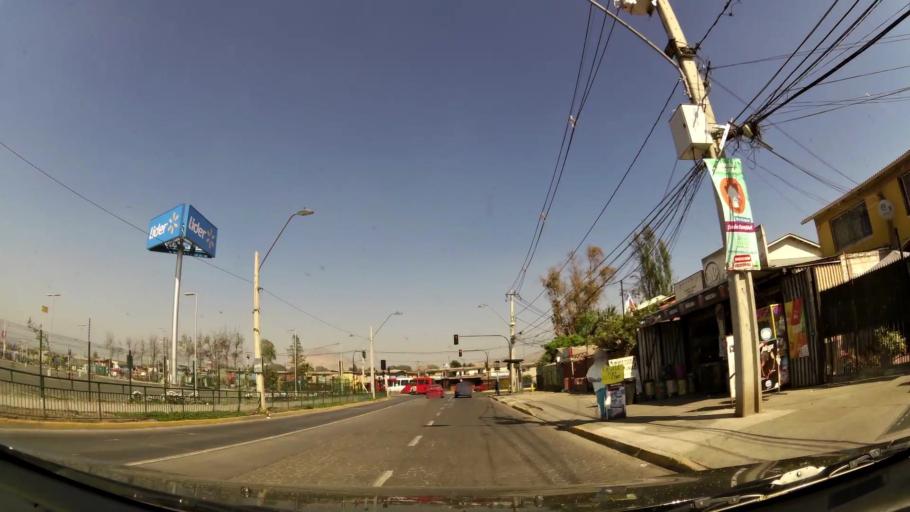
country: CL
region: Santiago Metropolitan
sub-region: Provincia de Santiago
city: Lo Prado
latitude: -33.3601
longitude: -70.7465
